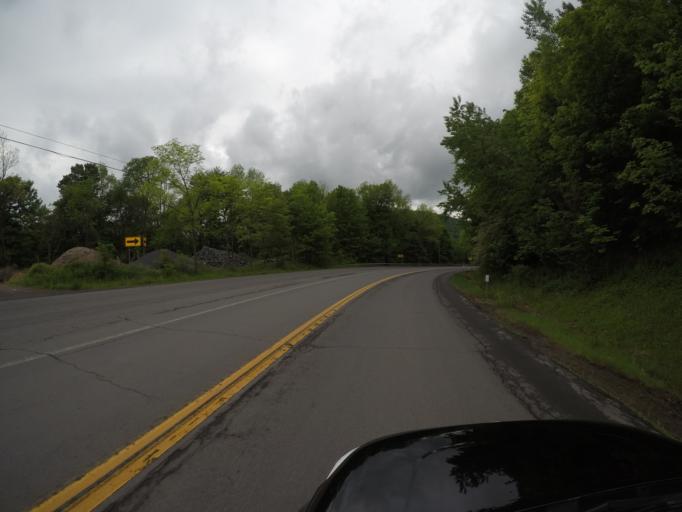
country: US
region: New York
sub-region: Delaware County
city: Delhi
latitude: 42.2561
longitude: -74.9216
